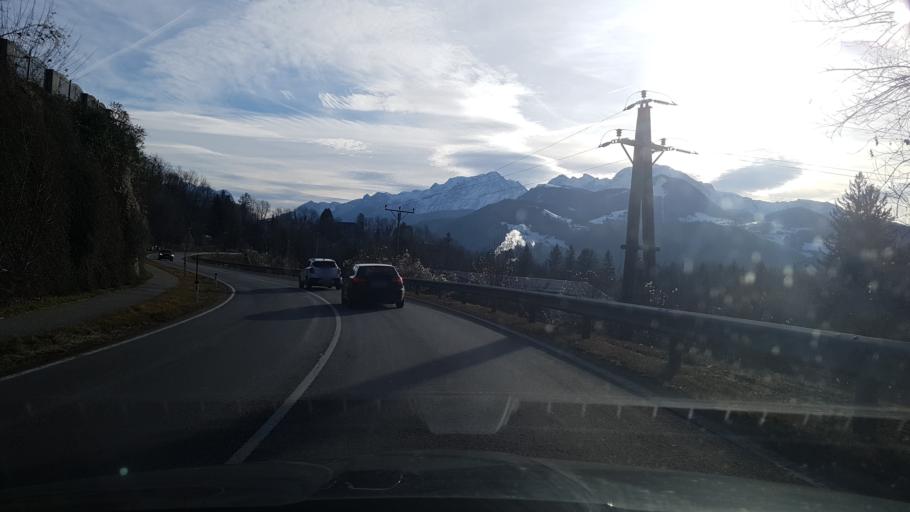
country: AT
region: Salzburg
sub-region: Politischer Bezirk Hallein
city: Oberalm
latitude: 47.6982
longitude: 13.1103
